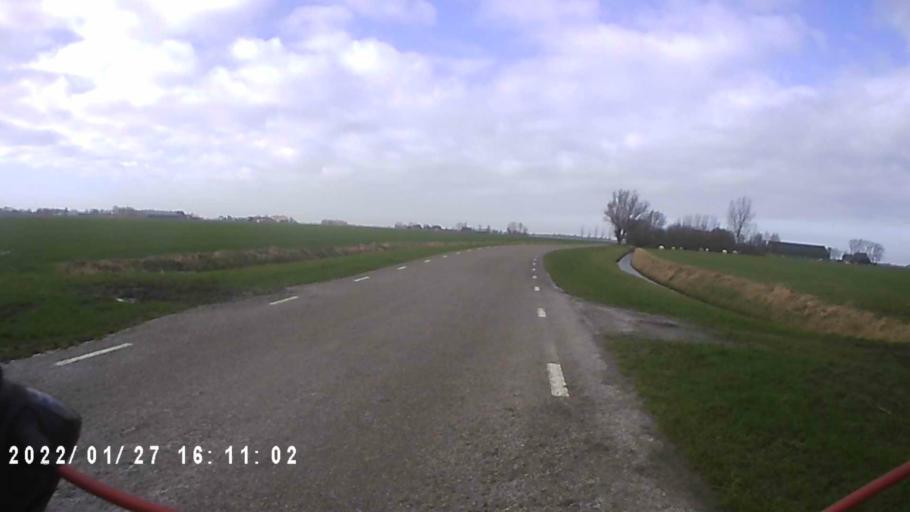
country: NL
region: Friesland
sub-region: Gemeente Dongeradeel
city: Anjum
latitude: 53.3828
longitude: 6.0788
